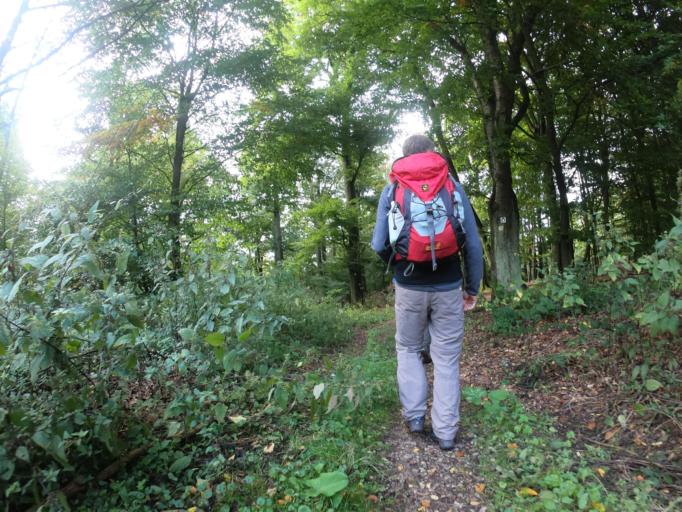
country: DE
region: Hesse
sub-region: Regierungsbezirk Darmstadt
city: Niedernhausen
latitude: 50.1374
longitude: 8.2840
